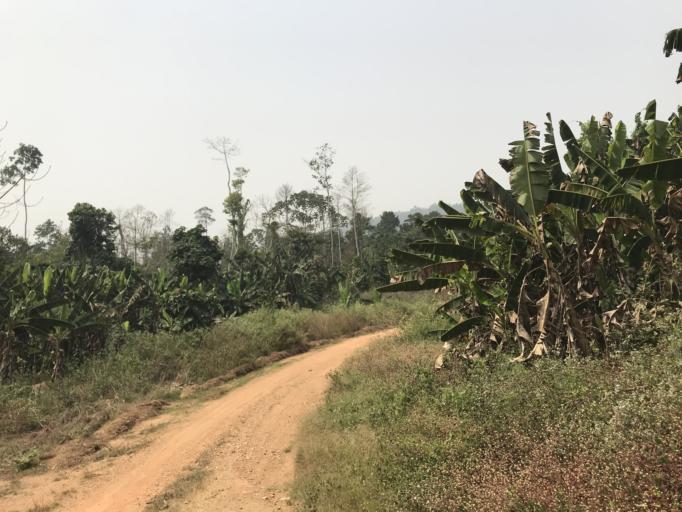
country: NG
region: Osun
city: Ifetedo
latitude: 7.0370
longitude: 4.4783
